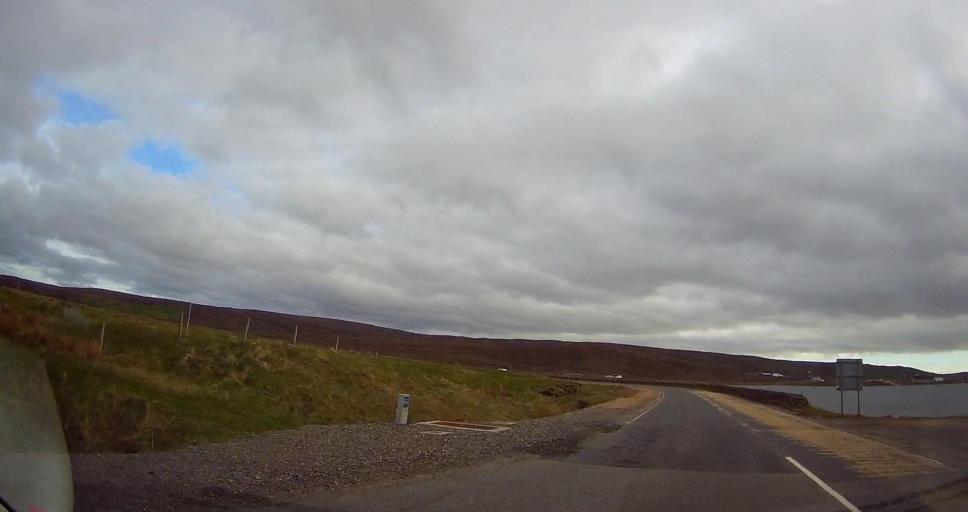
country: GB
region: Scotland
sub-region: Shetland Islands
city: Lerwick
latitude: 60.4489
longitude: -1.2592
